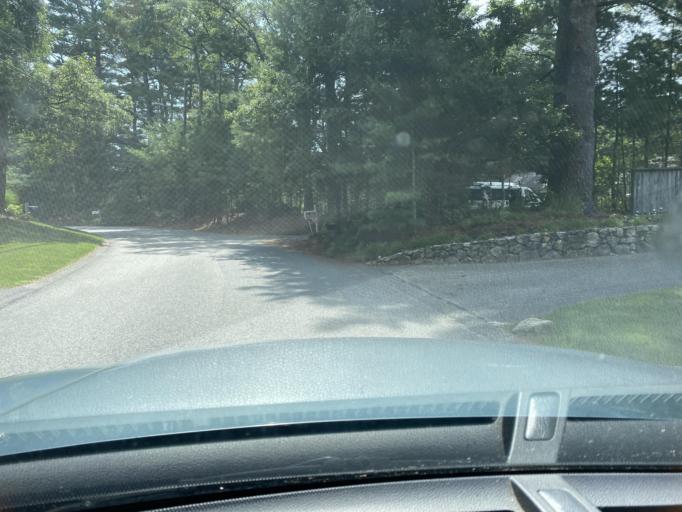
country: US
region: Massachusetts
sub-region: Barnstable County
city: Osterville
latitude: 41.6516
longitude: -70.3877
